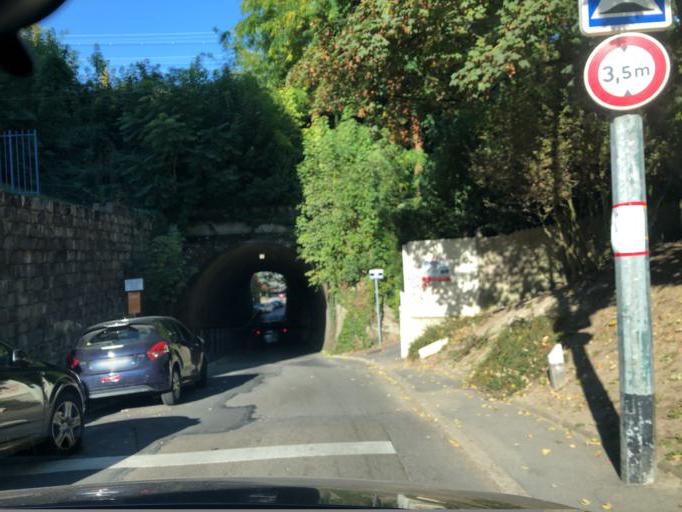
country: FR
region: Ile-de-France
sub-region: Departement des Hauts-de-Seine
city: Chaville
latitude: 48.8096
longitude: 2.1950
